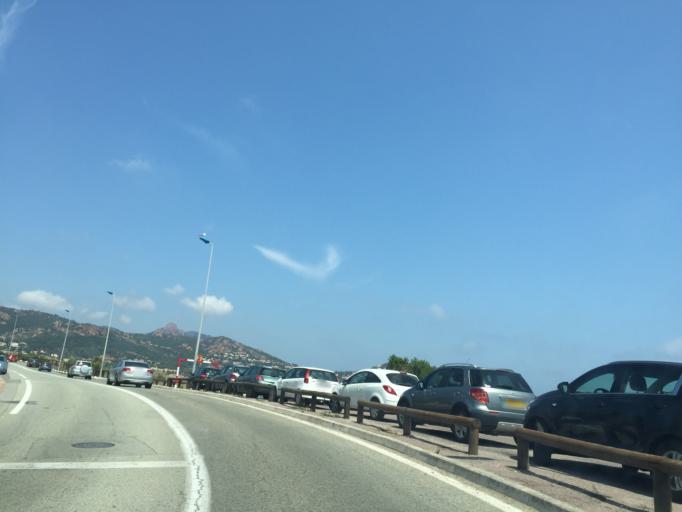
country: FR
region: Provence-Alpes-Cote d'Azur
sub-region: Departement du Var
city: Saint-Raphael
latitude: 43.4259
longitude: 6.8570
